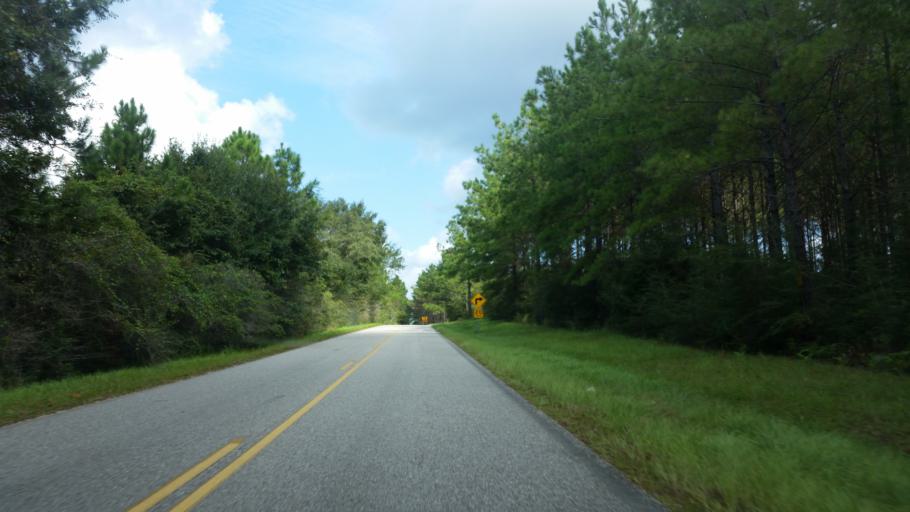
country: US
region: Florida
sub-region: Escambia County
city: Cantonment
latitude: 30.6783
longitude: -87.4704
